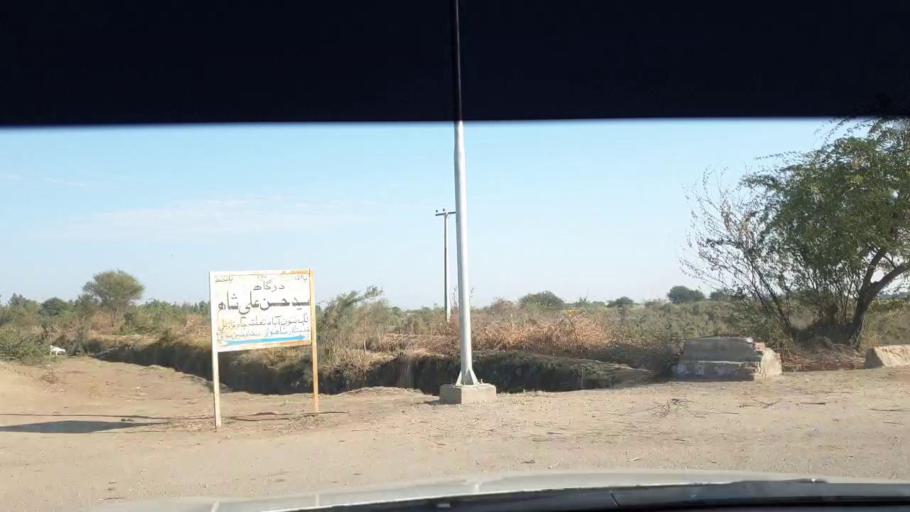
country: PK
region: Sindh
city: Berani
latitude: 25.8101
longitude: 68.9332
